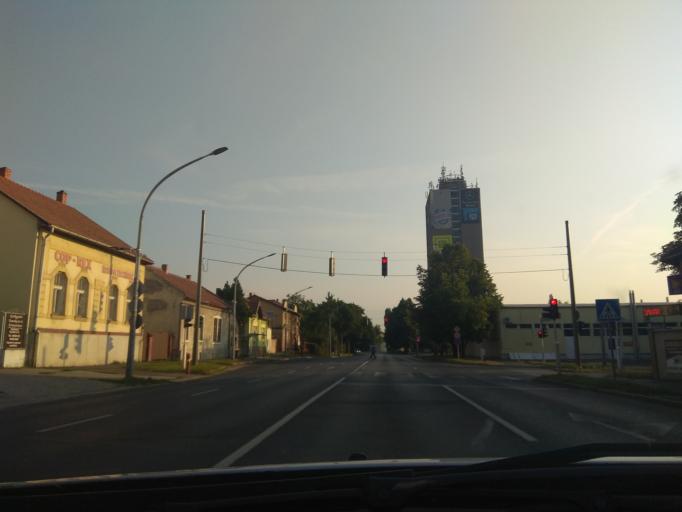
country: HU
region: Borsod-Abauj-Zemplen
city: Miskolc
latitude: 48.1136
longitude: 20.7893
